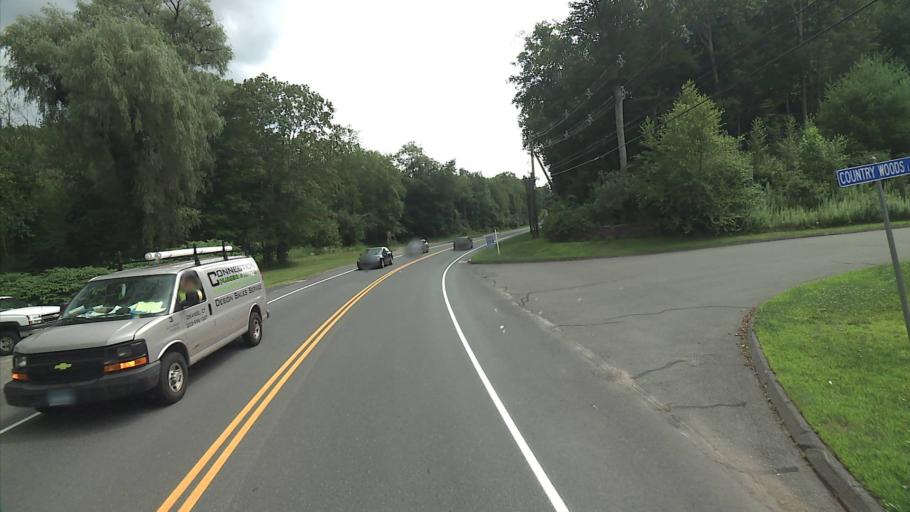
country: US
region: Connecticut
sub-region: New Haven County
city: Heritage Village
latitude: 41.5071
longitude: -73.2384
